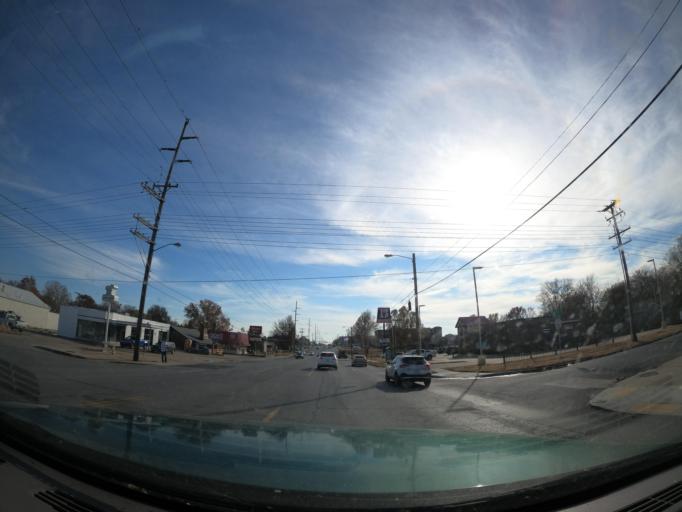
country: US
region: Oklahoma
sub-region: Tulsa County
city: Tulsa
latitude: 36.1226
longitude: -95.9403
